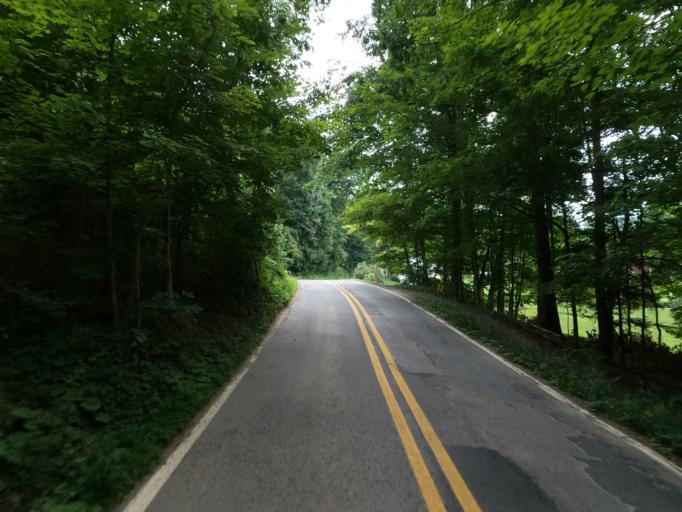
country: US
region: West Virginia
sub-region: Marion County
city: Fairmont
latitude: 39.4986
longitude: -80.0933
